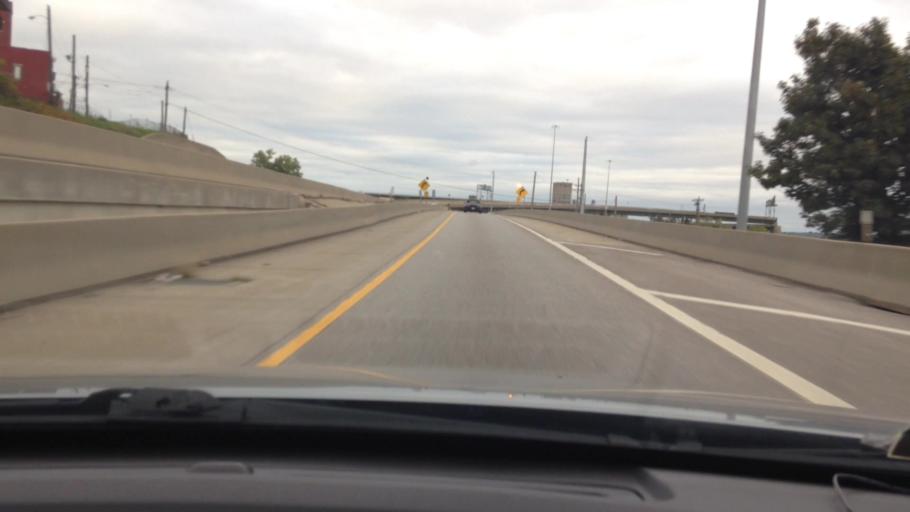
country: US
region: Kansas
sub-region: Wyandotte County
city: Kansas City
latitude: 39.1110
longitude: -94.6189
